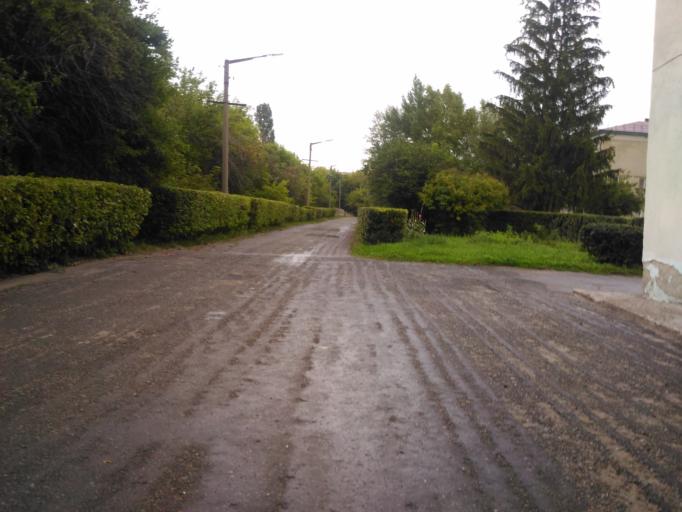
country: RU
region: Ulyanovsk
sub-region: Ulyanovskiy Rayon
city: Ulyanovsk
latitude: 54.2664
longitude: 48.3356
